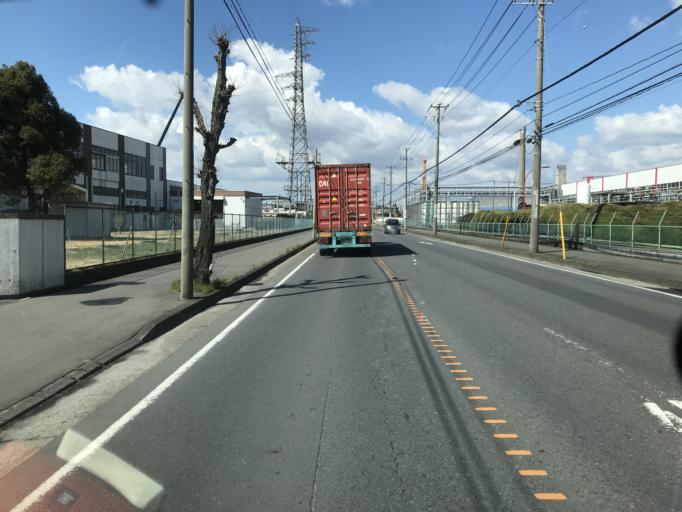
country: JP
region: Ibaraki
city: Ishioka
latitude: 36.1209
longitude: 140.2206
